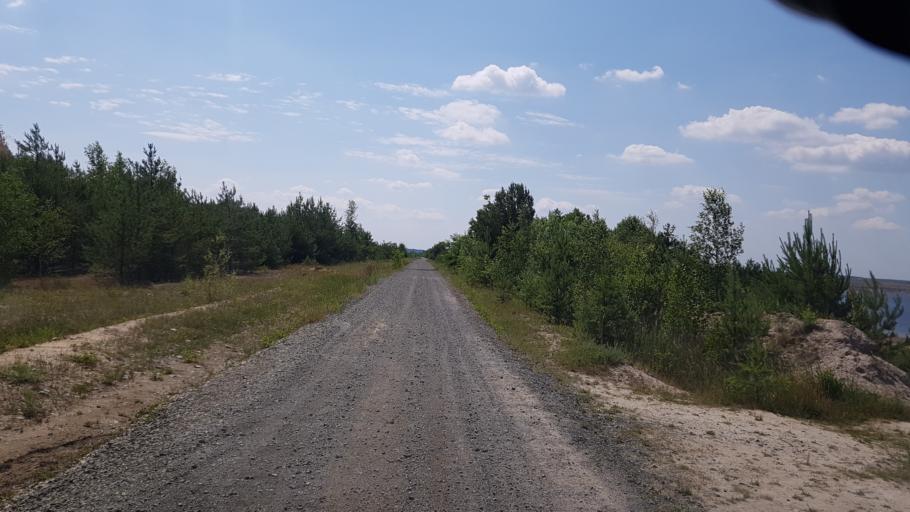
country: DE
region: Brandenburg
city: Sallgast
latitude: 51.5789
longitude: 13.8009
